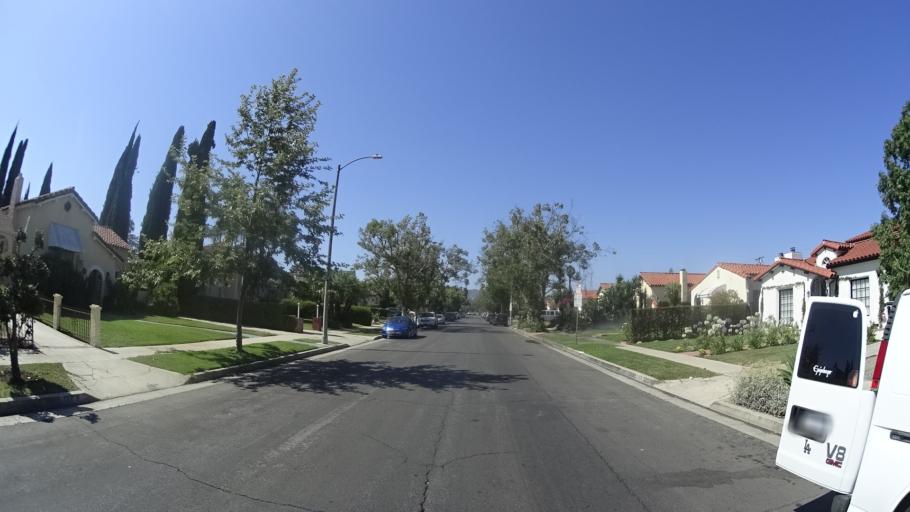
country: US
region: California
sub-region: Los Angeles County
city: West Hollywood
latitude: 34.0741
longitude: -118.3486
